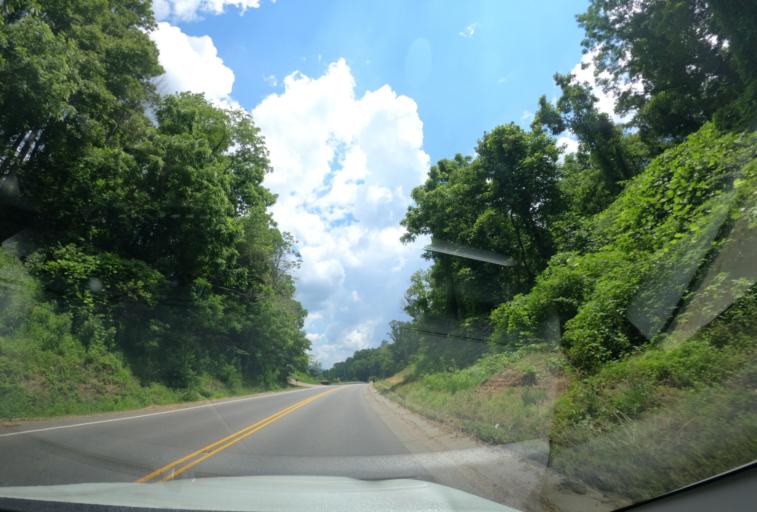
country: US
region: North Carolina
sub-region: Haywood County
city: Waynesville
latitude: 35.4729
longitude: -82.9394
